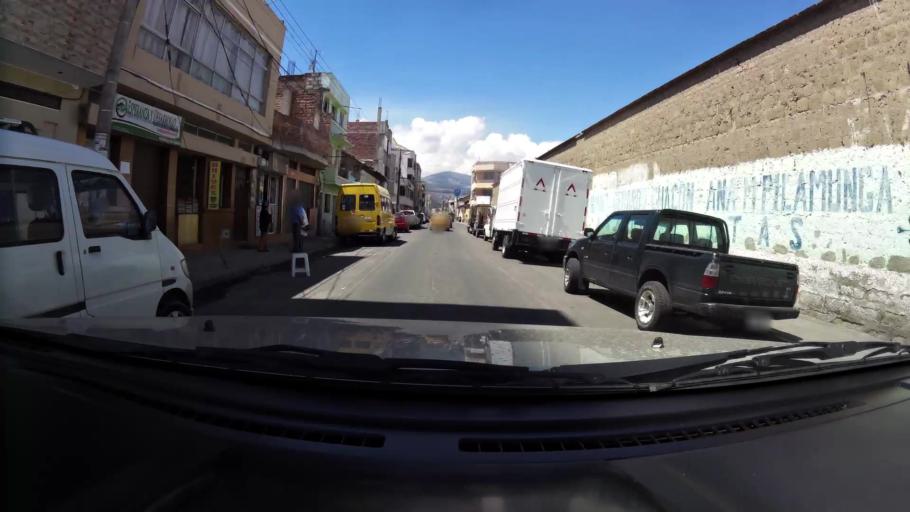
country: EC
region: Chimborazo
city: Riobamba
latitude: -1.6739
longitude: -78.6546
